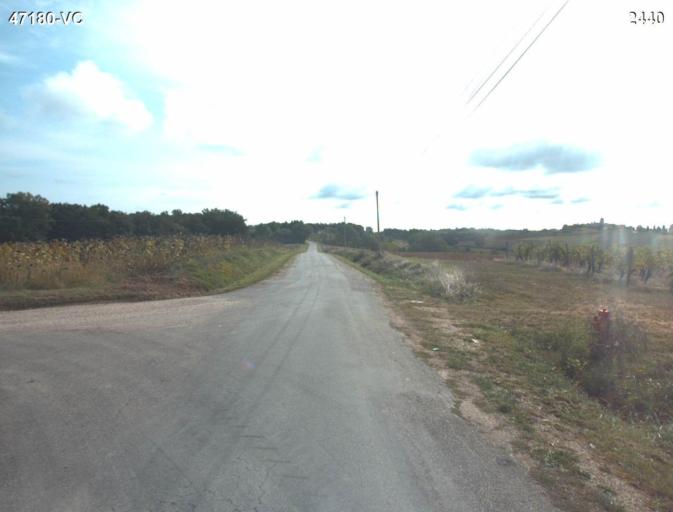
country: FR
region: Aquitaine
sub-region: Departement du Lot-et-Garonne
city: Sainte-Colombe-en-Bruilhois
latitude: 44.1706
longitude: 0.4454
